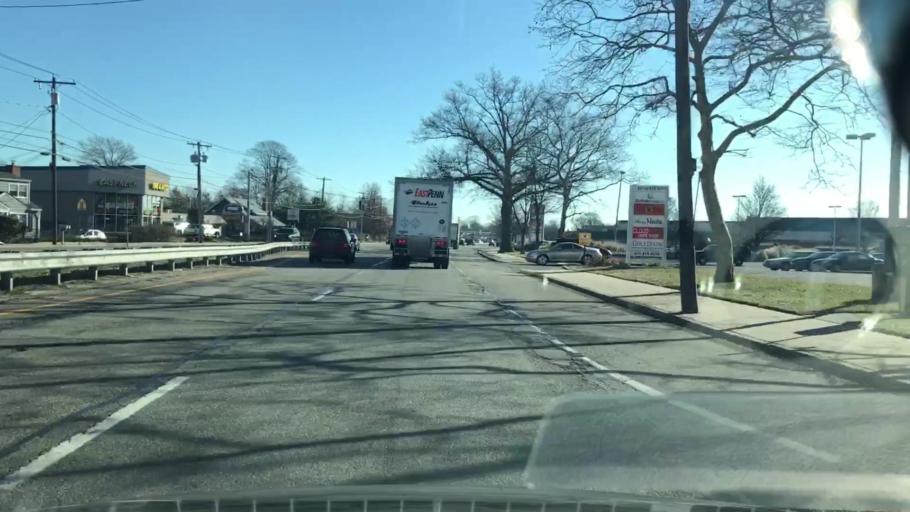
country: US
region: New York
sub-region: Suffolk County
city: West Babylon
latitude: 40.7061
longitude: -73.3484
